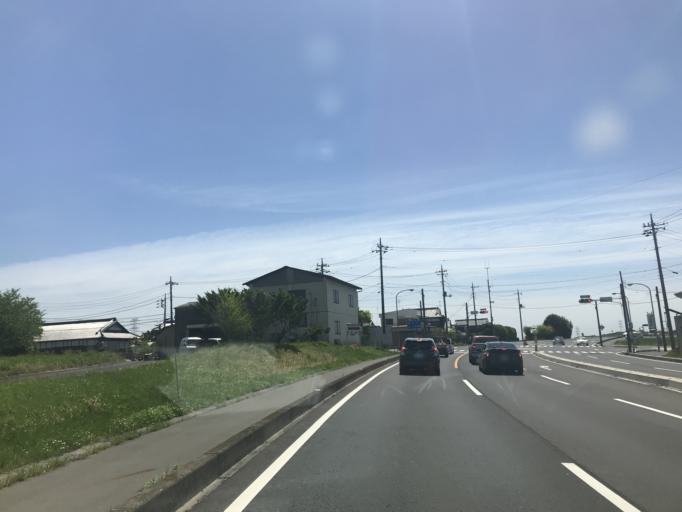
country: JP
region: Ibaraki
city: Shimodate
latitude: 36.2636
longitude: 139.9839
